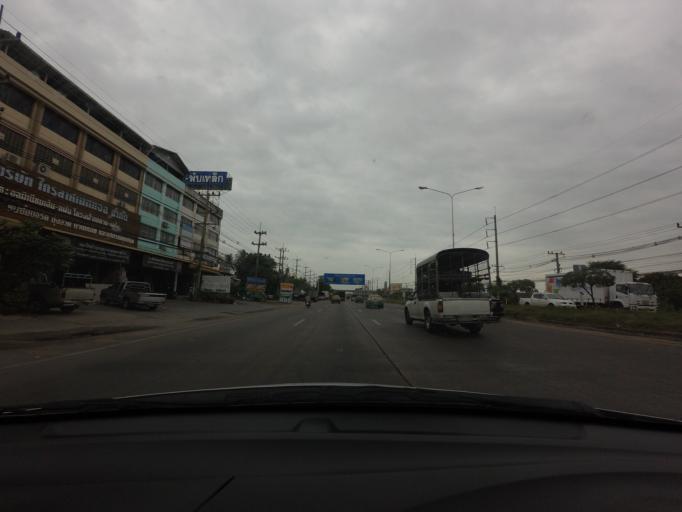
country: TH
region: Nakhon Pathom
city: Sam Phran
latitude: 13.7264
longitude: 100.2519
